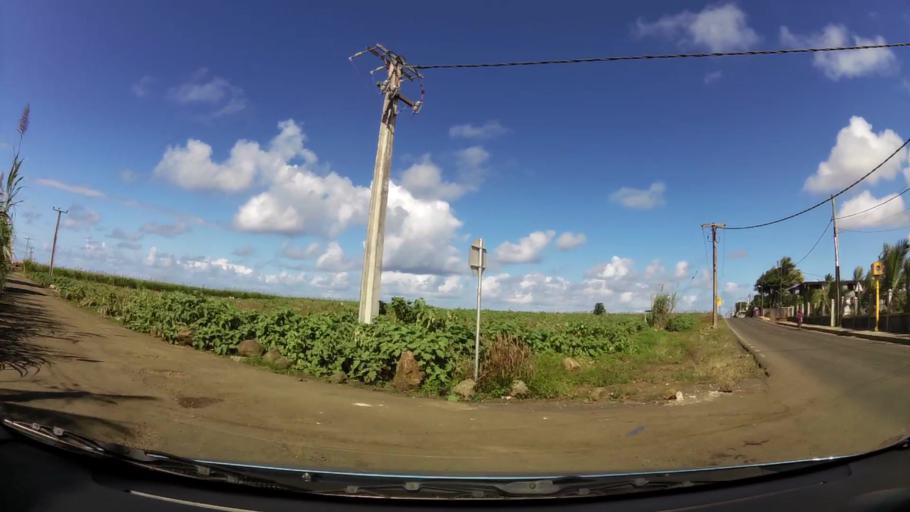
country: MU
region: Grand Port
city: Plaine Magnien
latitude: -20.4363
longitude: 57.6579
